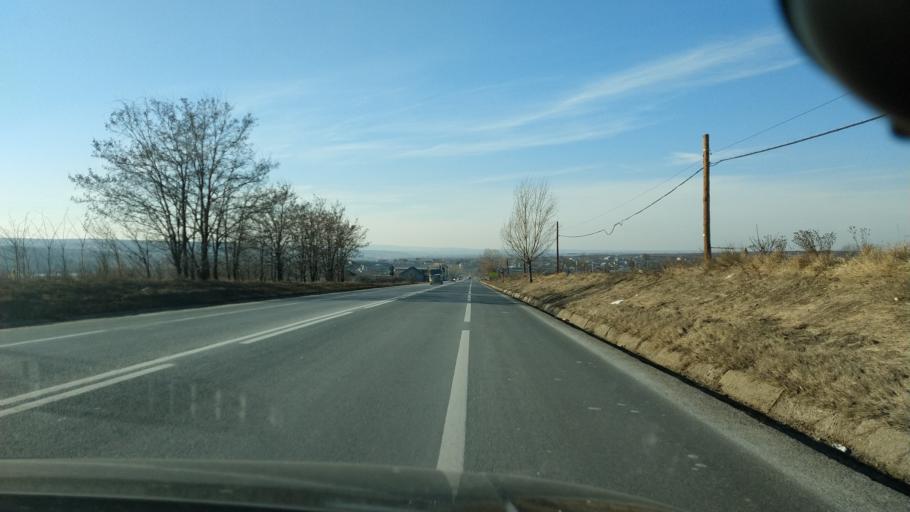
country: RO
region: Iasi
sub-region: Comuna Baltati
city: Baltati
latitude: 47.2203
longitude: 27.1334
